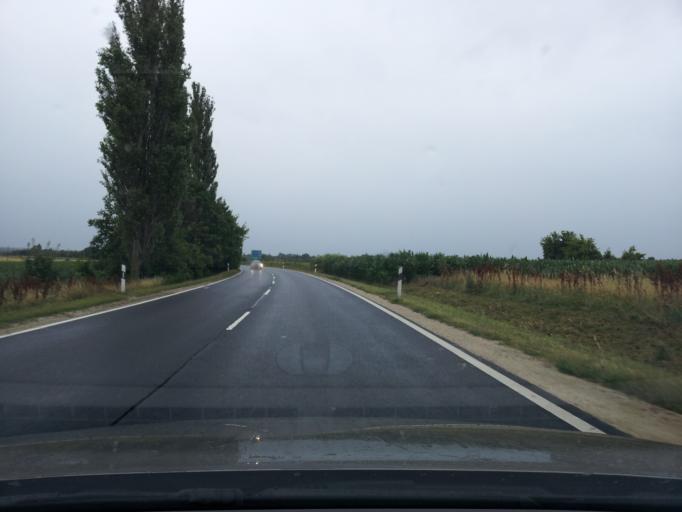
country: HU
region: Fejer
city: Lepseny
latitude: 46.9980
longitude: 18.1799
